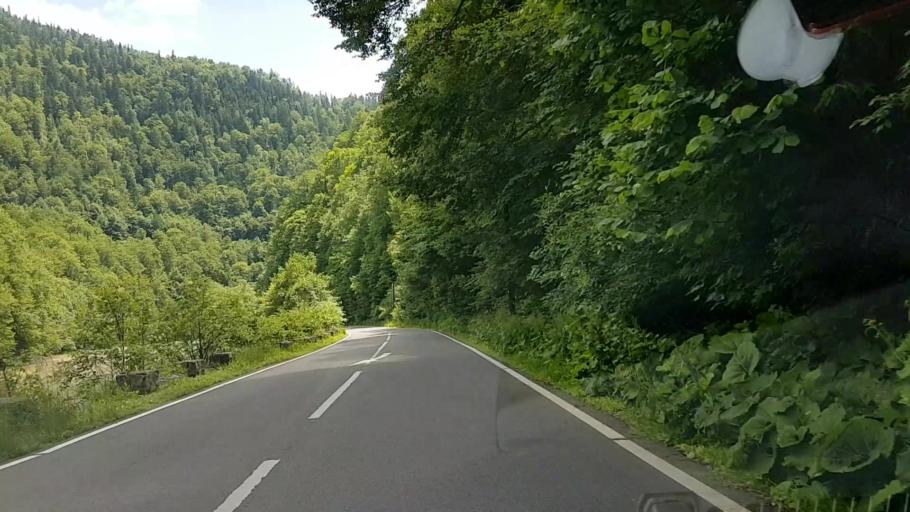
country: RO
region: Suceava
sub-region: Comuna Crucea
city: Crucea
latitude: 47.3138
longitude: 25.6261
